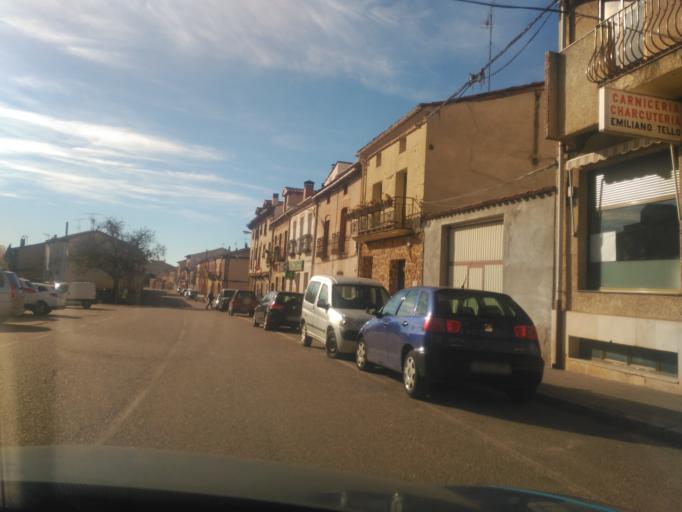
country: ES
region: Castille and Leon
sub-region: Provincia de Burgos
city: Huerta del Rey
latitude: 41.8397
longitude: -3.3461
